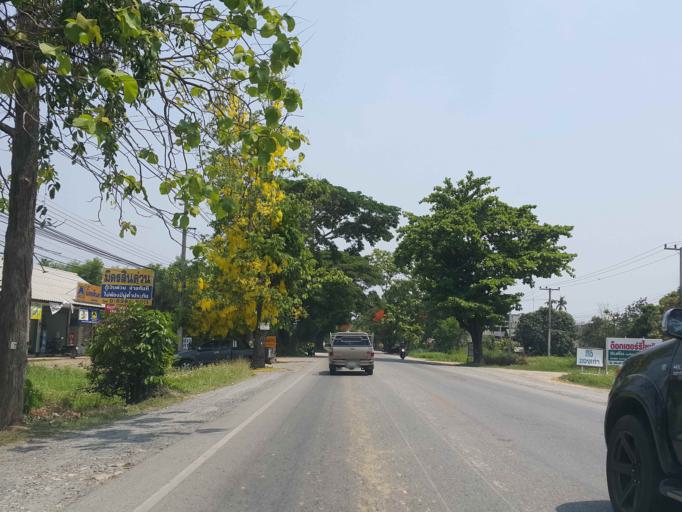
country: TH
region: Chiang Mai
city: San Sai
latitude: 18.9684
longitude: 98.9834
